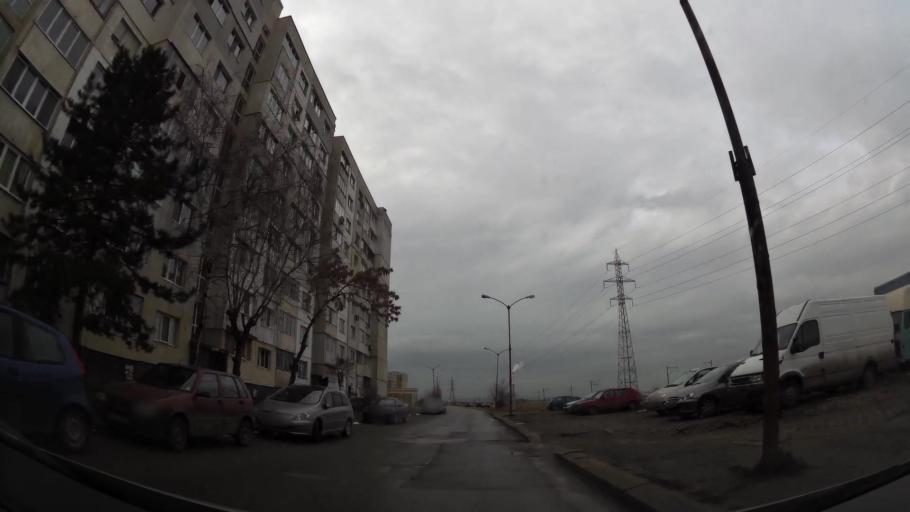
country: BG
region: Sofia-Capital
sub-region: Stolichna Obshtina
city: Sofia
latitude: 42.7483
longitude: 23.2741
